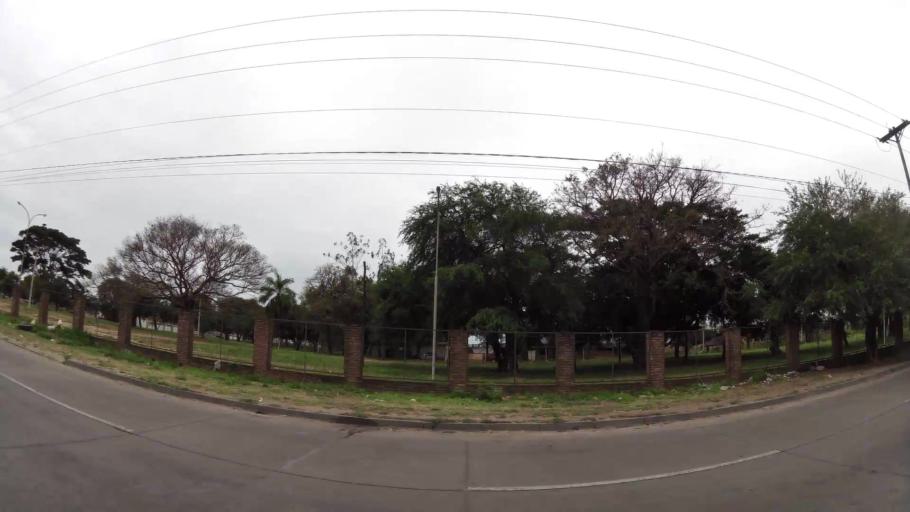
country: BO
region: Santa Cruz
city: Santa Cruz de la Sierra
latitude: -17.8226
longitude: -63.1875
